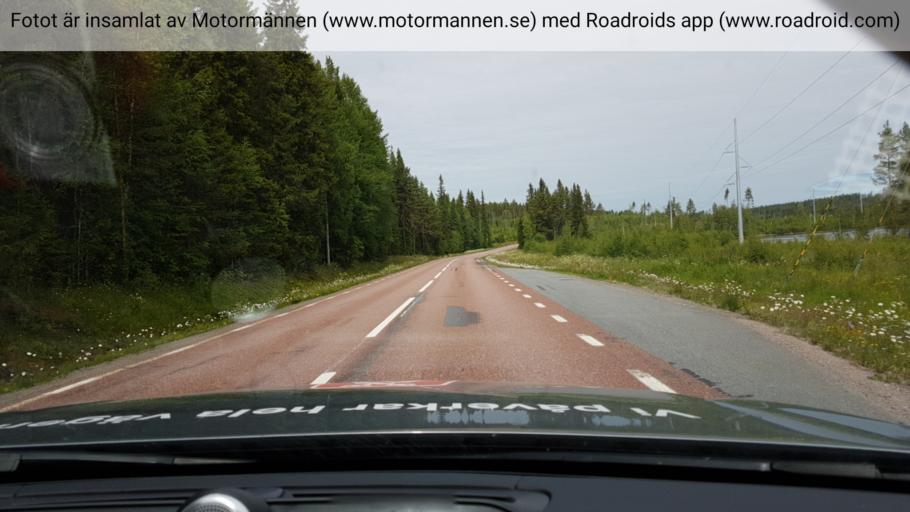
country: SE
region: Vaesterbotten
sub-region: Dorotea Kommun
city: Dorotea
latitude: 64.0588
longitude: 16.0452
